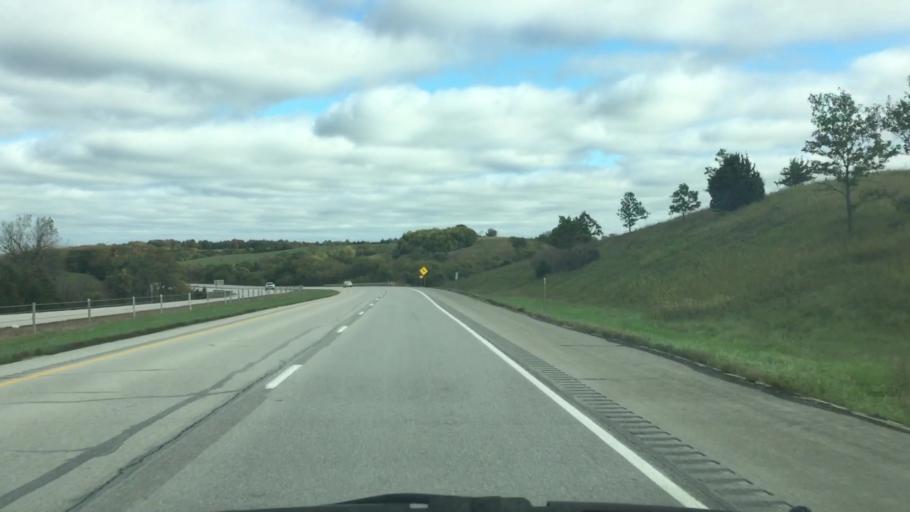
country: US
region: Iowa
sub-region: Clarke County
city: Osceola
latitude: 41.0502
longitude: -93.7836
